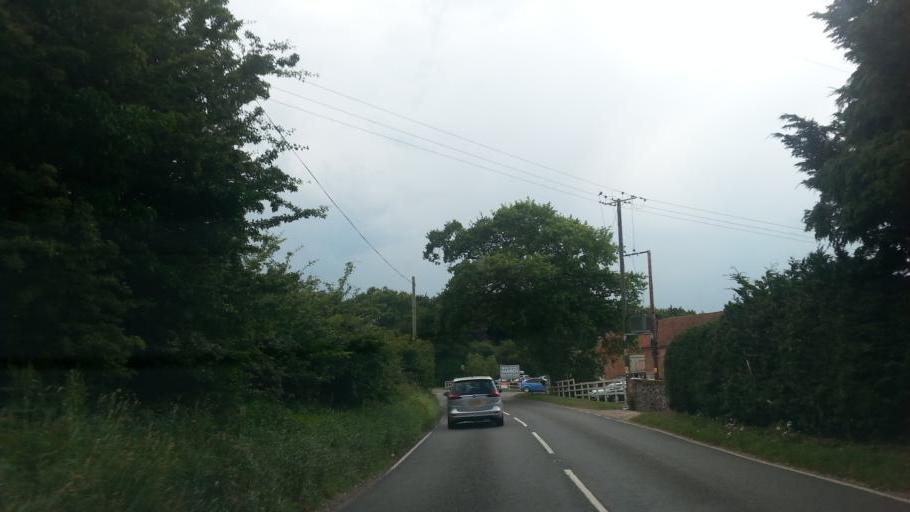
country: GB
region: England
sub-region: Norfolk
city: Briston
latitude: 52.9038
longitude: 1.0440
